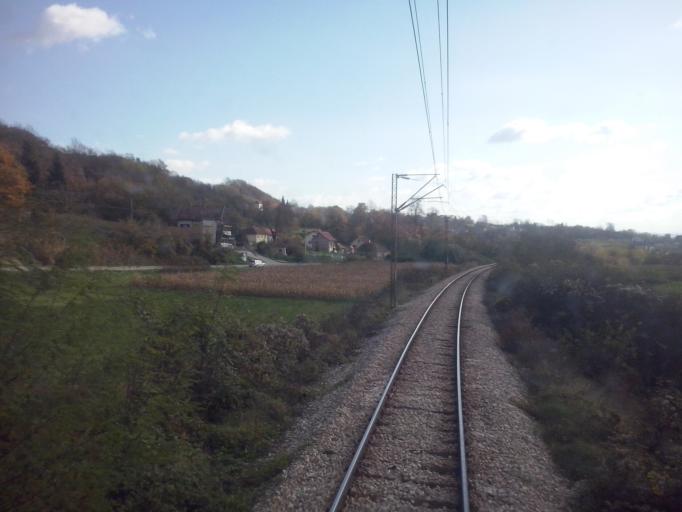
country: RS
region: Central Serbia
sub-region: Zlatiborski Okrug
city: Pozega
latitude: 43.8711
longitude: 20.0060
